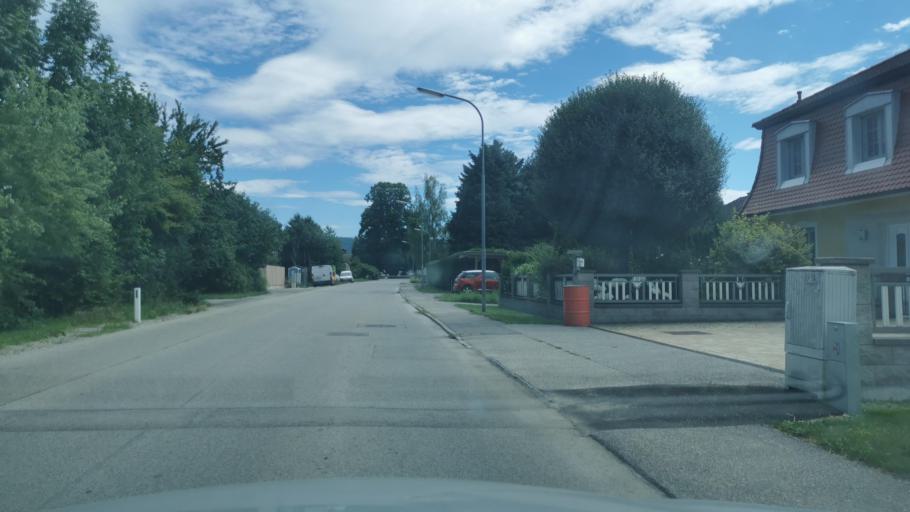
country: AT
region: Lower Austria
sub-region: Sankt Polten Stadt
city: Sankt Poelten
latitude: 48.1602
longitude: 15.6398
